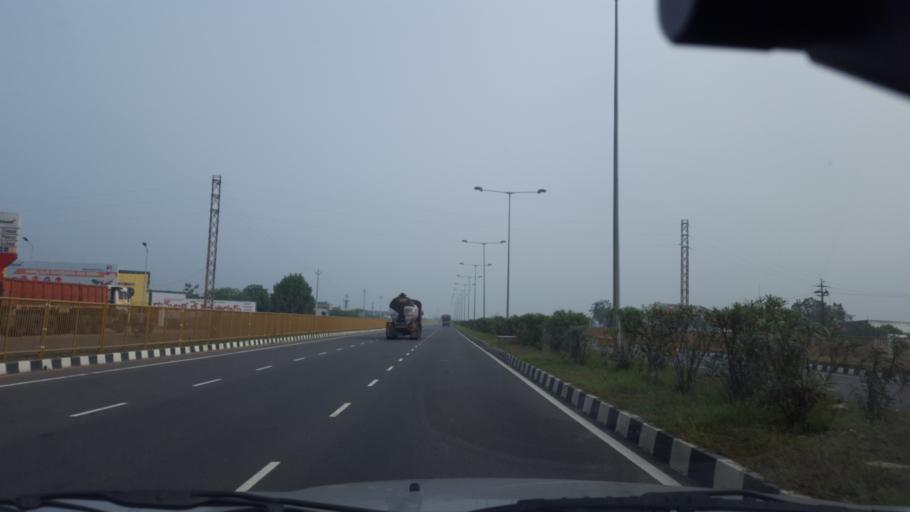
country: IN
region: Andhra Pradesh
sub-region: Guntur
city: Chilakalurupet
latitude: 16.0014
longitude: 80.1118
